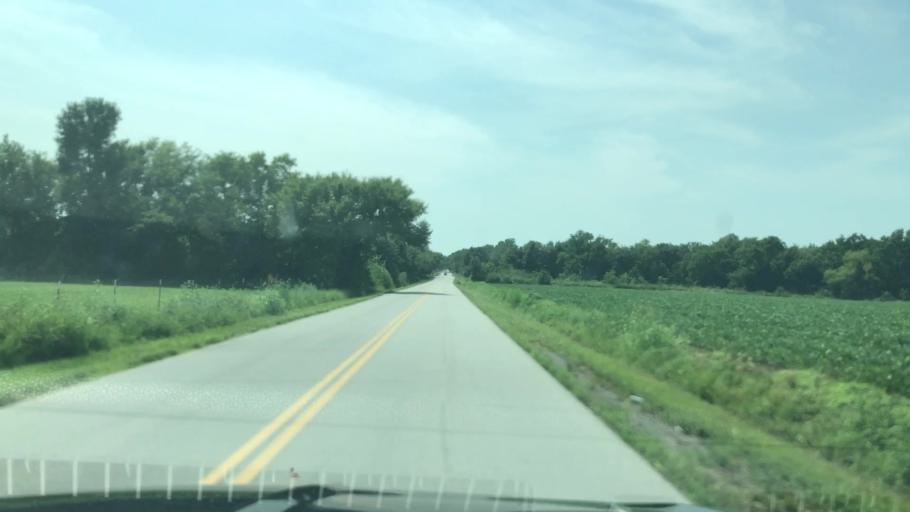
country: US
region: Oklahoma
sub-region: Ottawa County
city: Commerce
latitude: 36.9292
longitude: -94.8545
